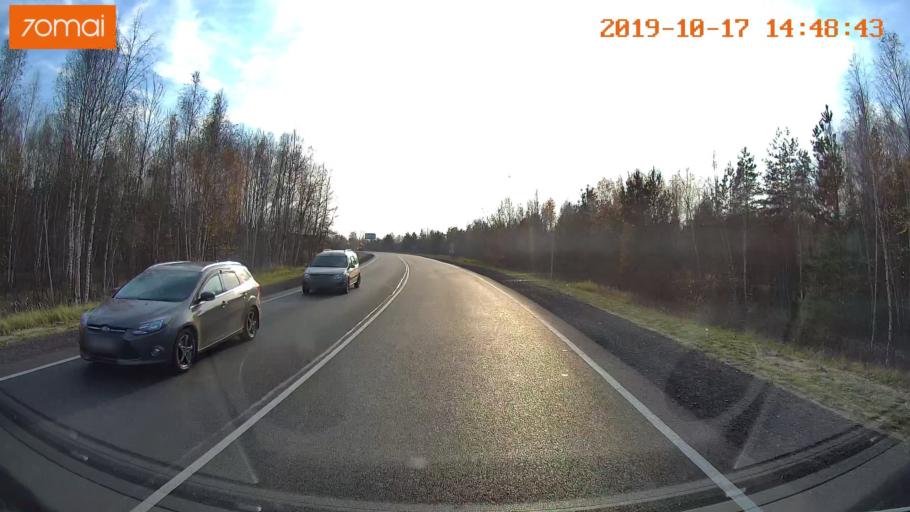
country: RU
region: Rjazan
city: Solotcha
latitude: 54.7560
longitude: 39.8403
